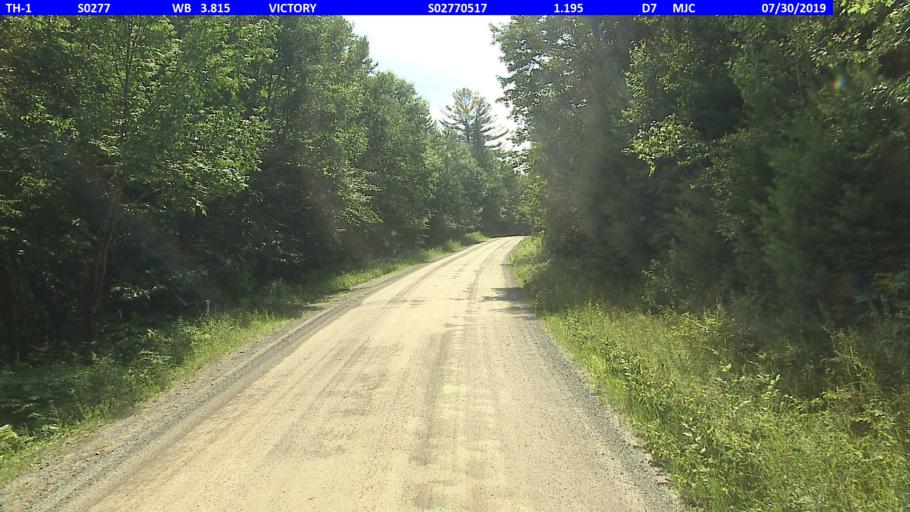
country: US
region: Vermont
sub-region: Caledonia County
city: Lyndonville
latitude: 44.5115
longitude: -71.8388
